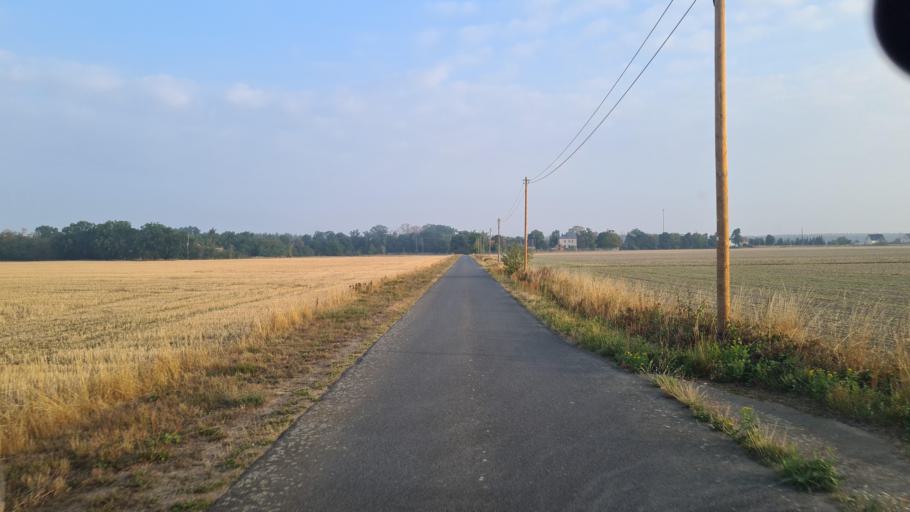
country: DE
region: Saxony
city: Arzberg
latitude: 51.5751
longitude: 13.1536
